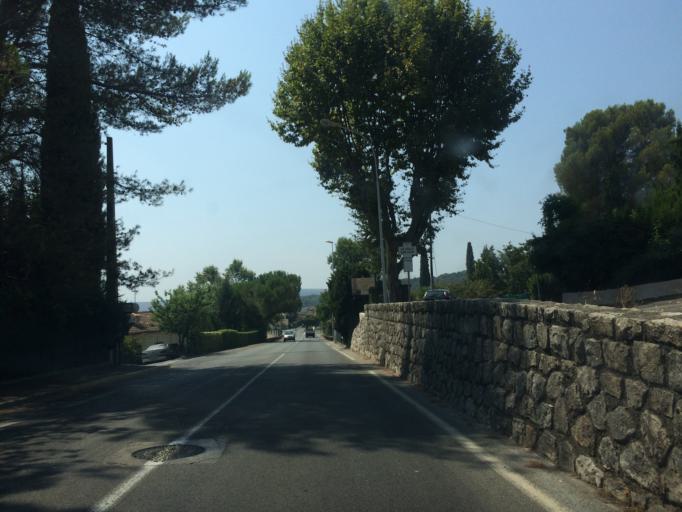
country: FR
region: Provence-Alpes-Cote d'Azur
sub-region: Departement des Alpes-Maritimes
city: La Colle-sur-Loup
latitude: 43.6932
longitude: 7.1059
